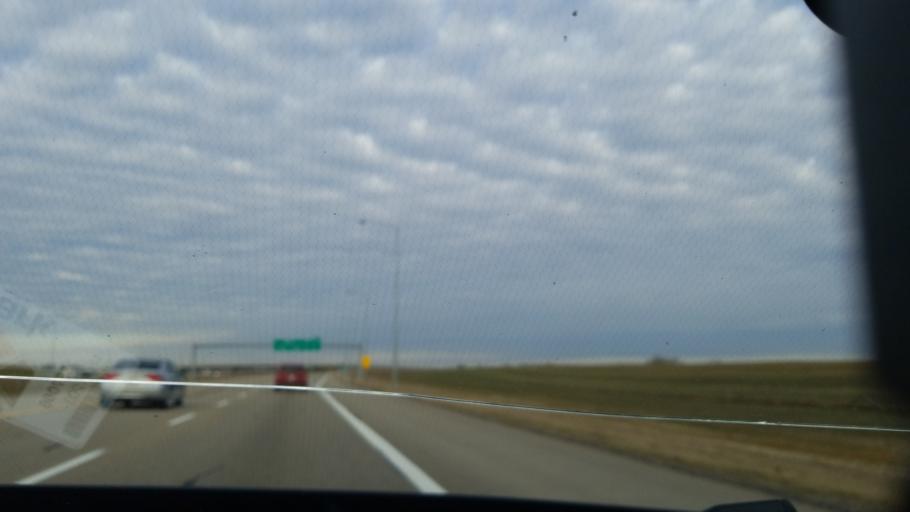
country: CA
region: Alberta
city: Edmonton
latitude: 53.6438
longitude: -113.4264
